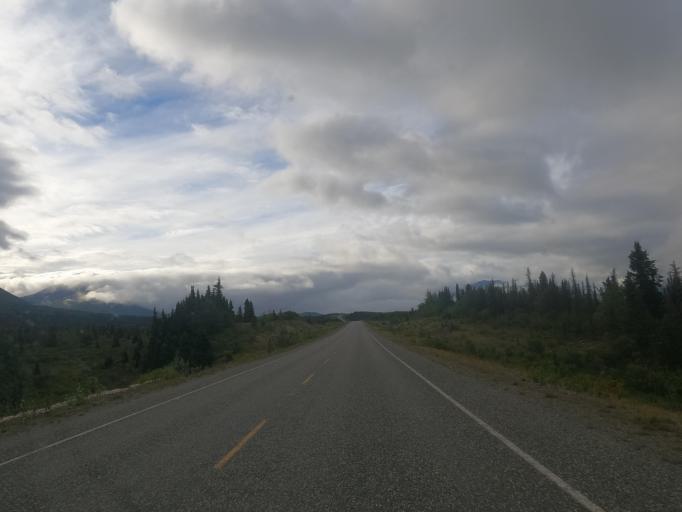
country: CA
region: Yukon
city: Haines Junction
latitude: 59.9625
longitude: -136.8141
